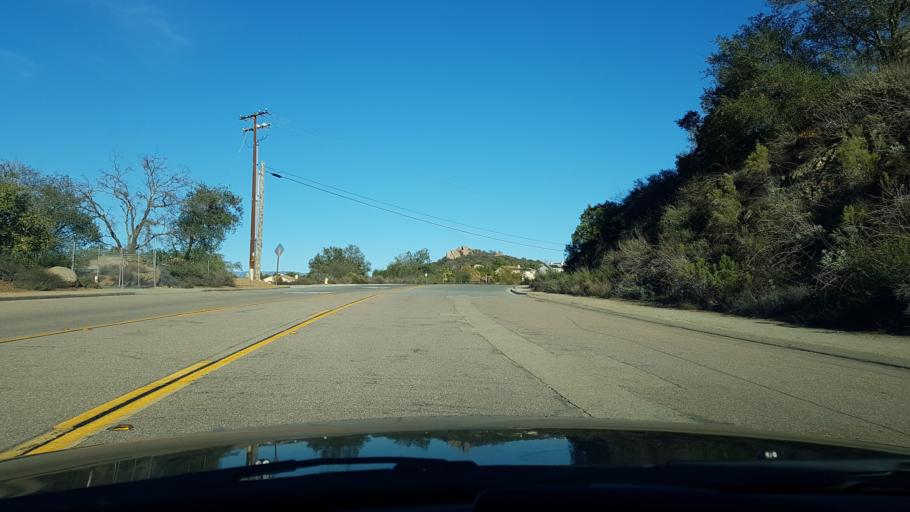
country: US
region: California
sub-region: San Diego County
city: Hidden Meadows
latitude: 33.2112
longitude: -117.1076
